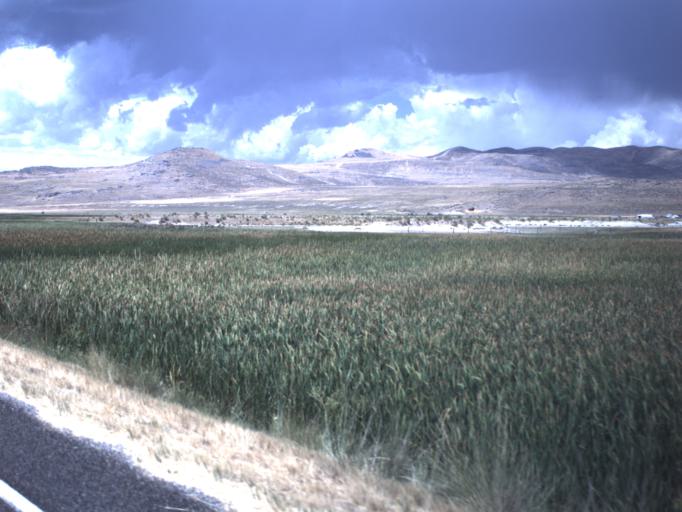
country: US
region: Utah
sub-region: Box Elder County
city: Tremonton
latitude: 41.6094
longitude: -112.3360
